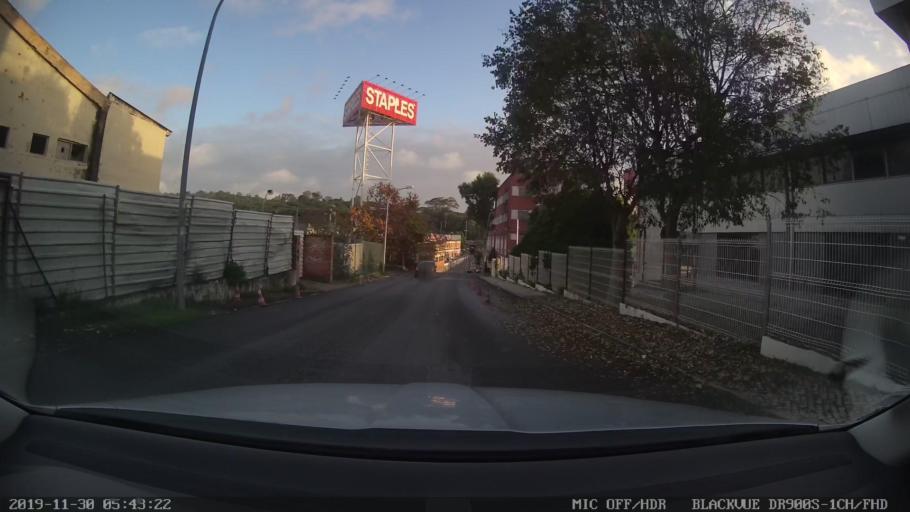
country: PT
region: Lisbon
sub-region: Oeiras
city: Alges
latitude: 38.7220
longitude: -9.2170
